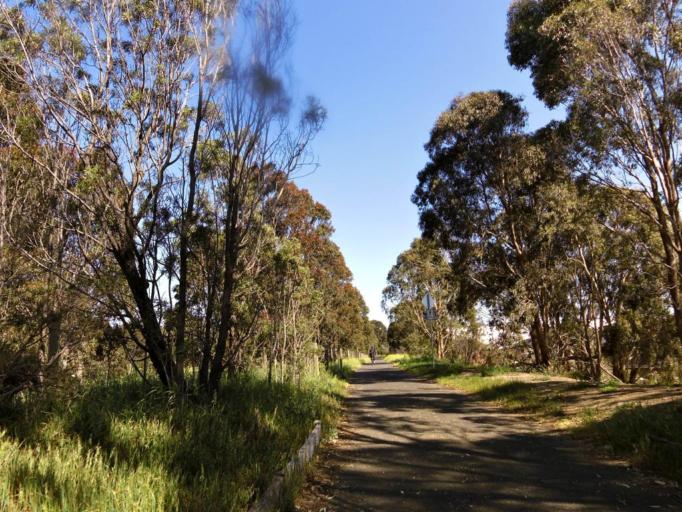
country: AU
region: Victoria
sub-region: Banyule
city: Watsonia North
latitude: -37.6874
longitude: 145.0784
